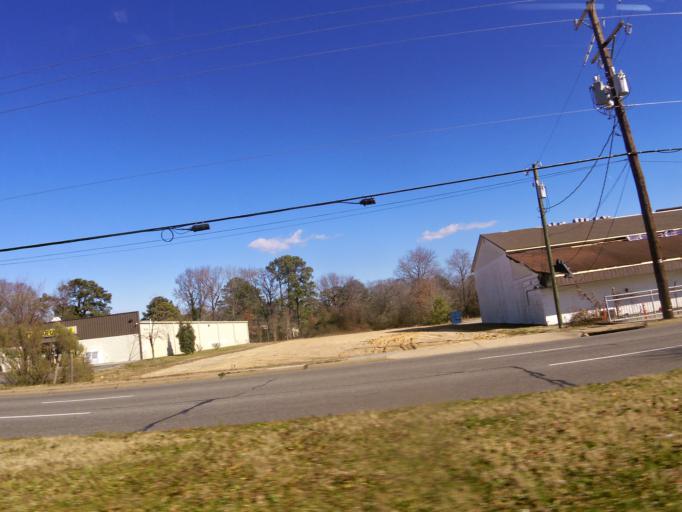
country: US
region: Virginia
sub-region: City of Newport News
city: Newport News
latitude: 37.0096
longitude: -76.4385
